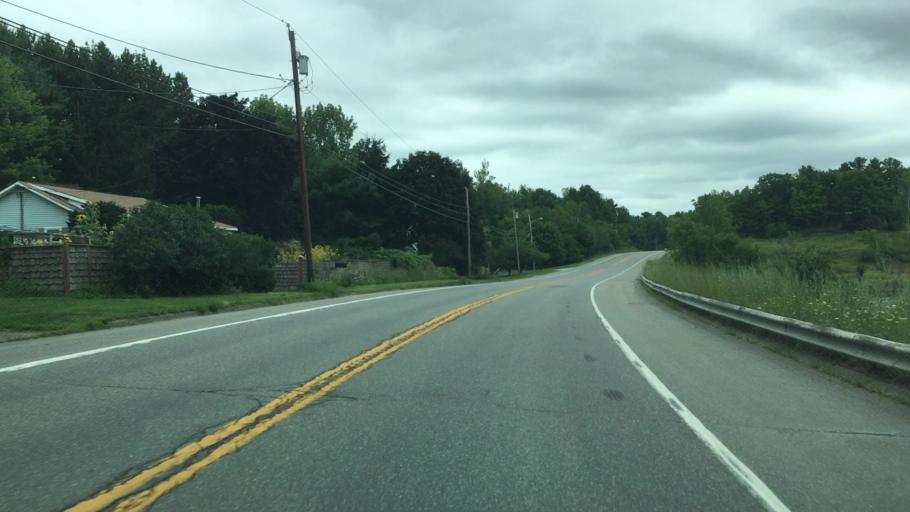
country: US
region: Maine
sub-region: Penobscot County
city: Orrington
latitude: 44.6957
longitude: -68.8474
